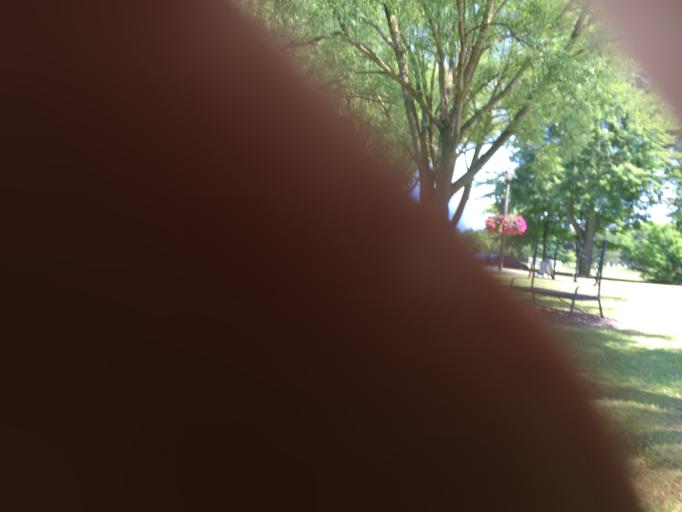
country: CA
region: Ontario
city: Stratford
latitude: 43.3755
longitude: -80.9704
